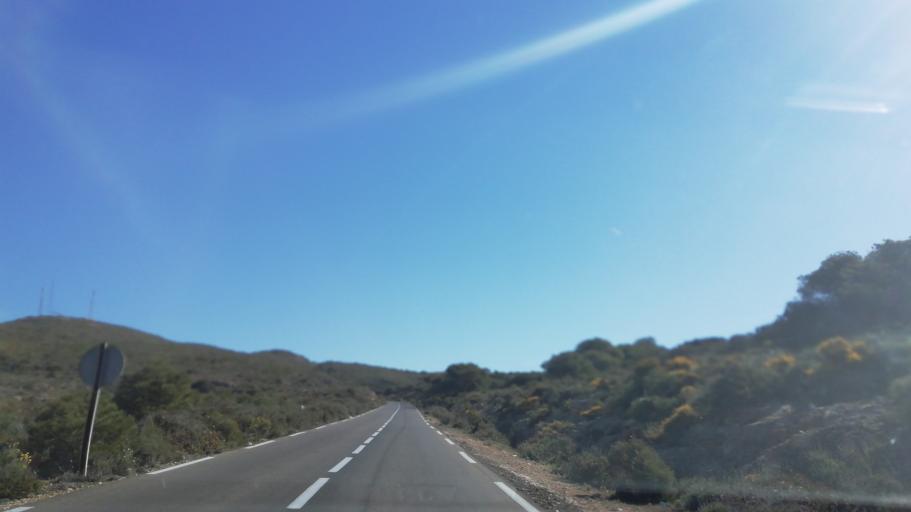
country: DZ
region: Ain Temouchent
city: El Amria
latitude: 35.6479
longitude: -1.0439
